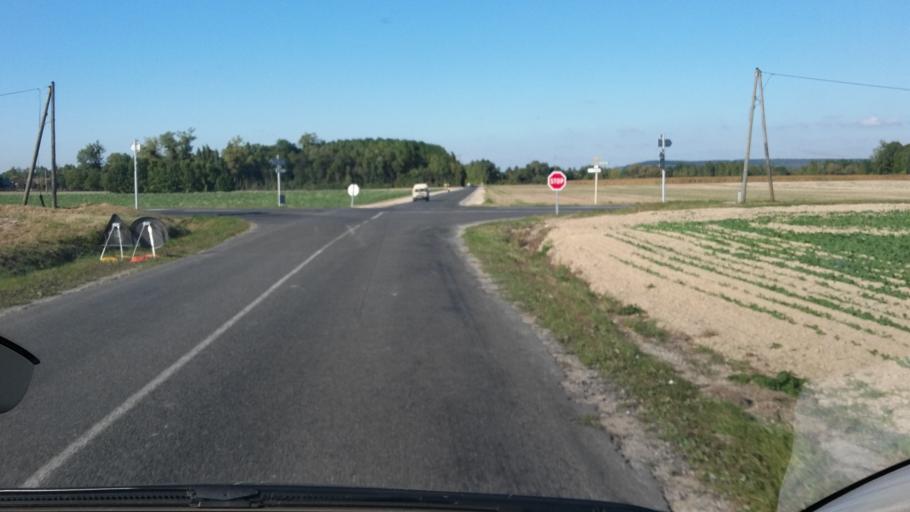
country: FR
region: Champagne-Ardenne
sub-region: Departement de la Marne
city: Connantre
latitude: 48.7852
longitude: 3.8620
